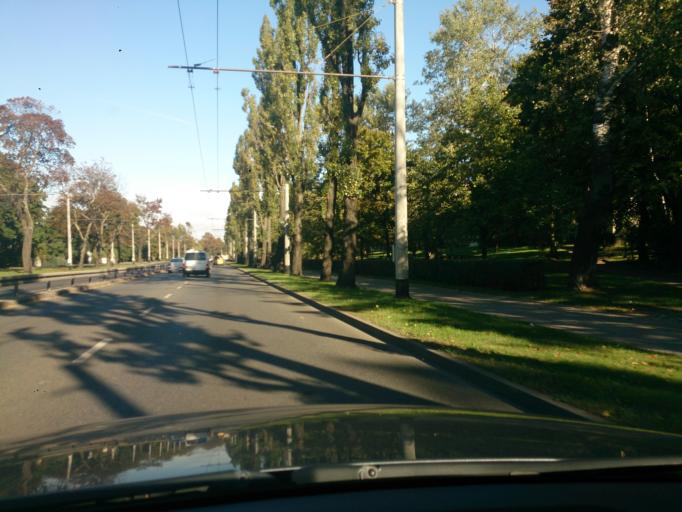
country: PL
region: Pomeranian Voivodeship
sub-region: Gdynia
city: Gdynia
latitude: 54.4989
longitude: 18.5377
